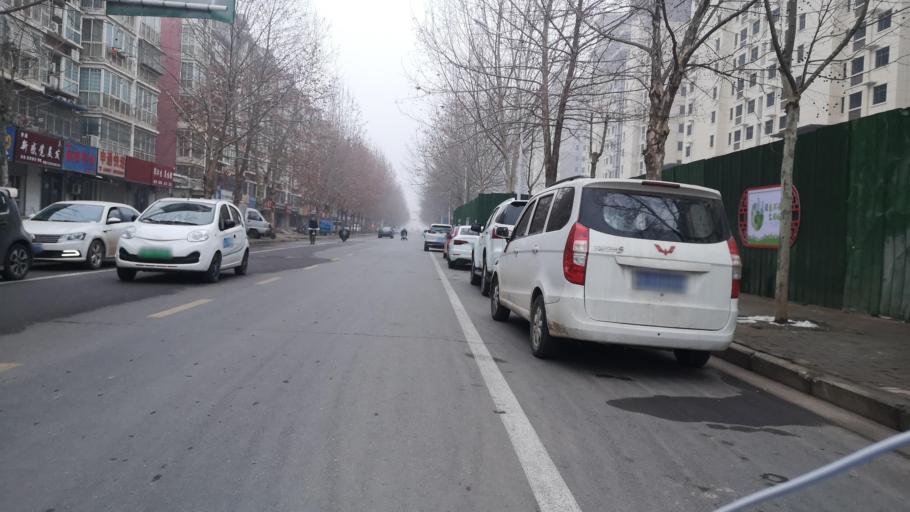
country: CN
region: Henan Sheng
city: Zhongyuanlu
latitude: 35.7640
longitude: 115.0798
